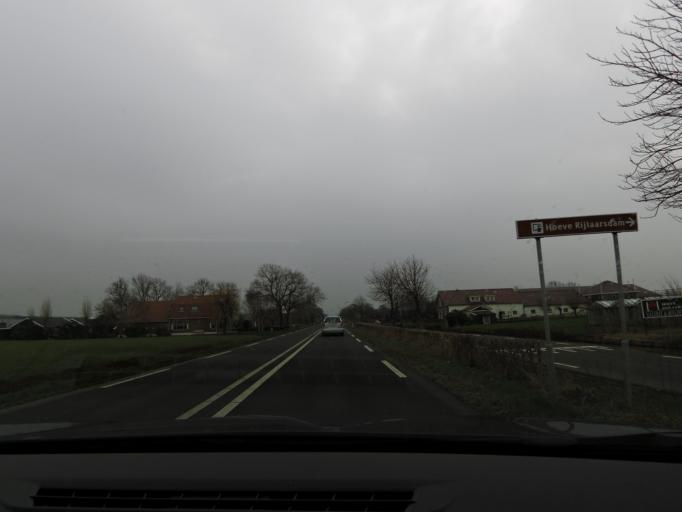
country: NL
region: South Holland
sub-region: Gemeente Nieuwkoop
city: Nieuwkoop
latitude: 52.1675
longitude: 4.7751
